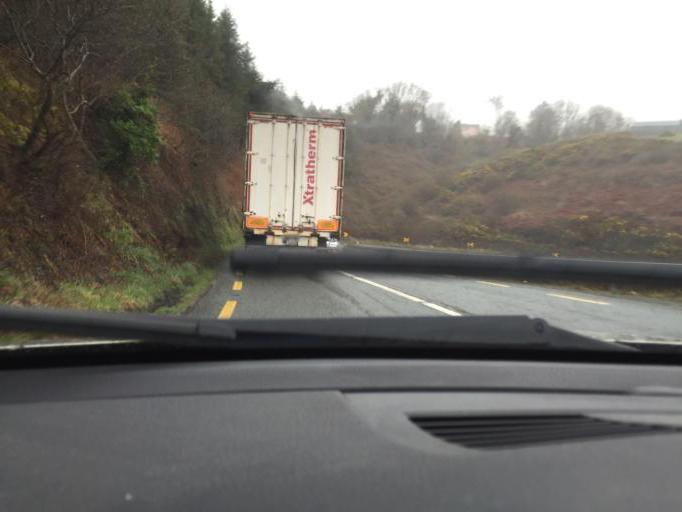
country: IE
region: Munster
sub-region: Ciarrai
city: Dingle
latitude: 52.1458
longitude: -10.0904
